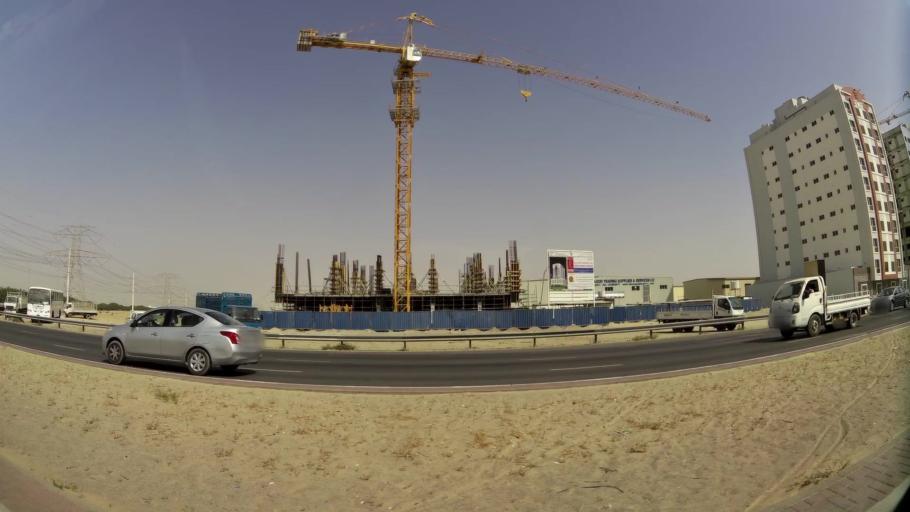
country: AE
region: Ash Shariqah
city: Sharjah
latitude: 25.2932
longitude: 55.4057
